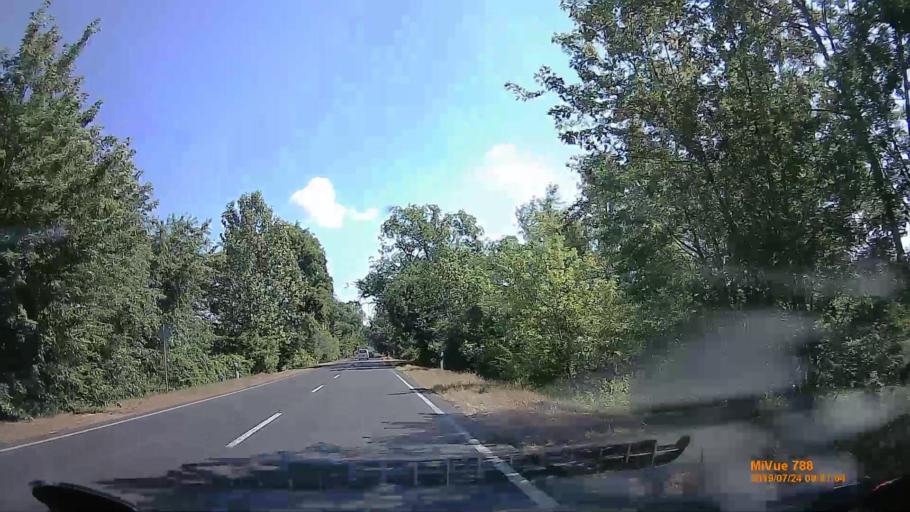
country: HU
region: Szabolcs-Szatmar-Bereg
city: Vaja
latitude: 48.0275
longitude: 22.1622
